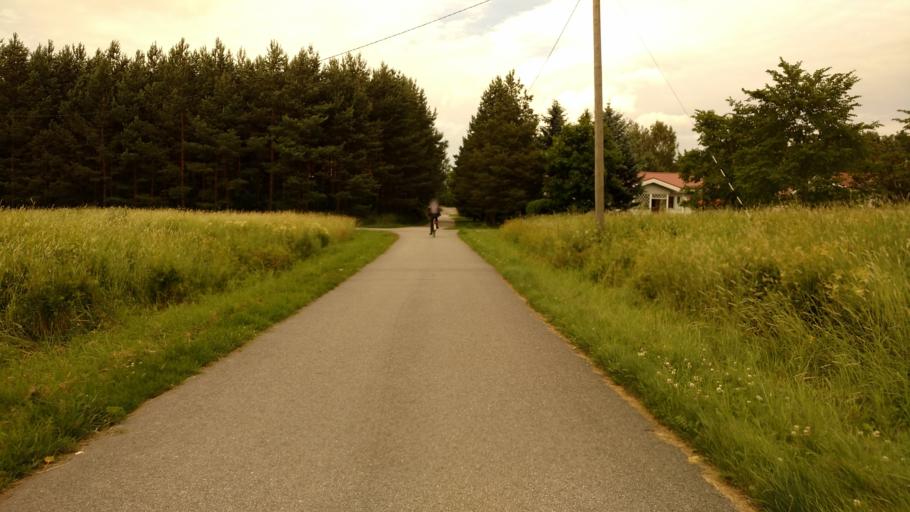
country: FI
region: Varsinais-Suomi
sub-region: Salo
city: Salo
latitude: 60.3901
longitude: 23.1660
